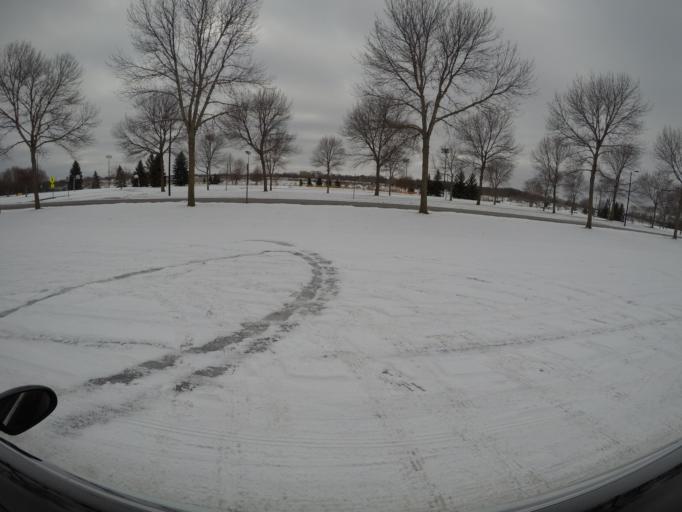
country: US
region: Minnesota
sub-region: Hennepin County
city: Eden Prairie
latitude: 44.8526
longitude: -93.4950
